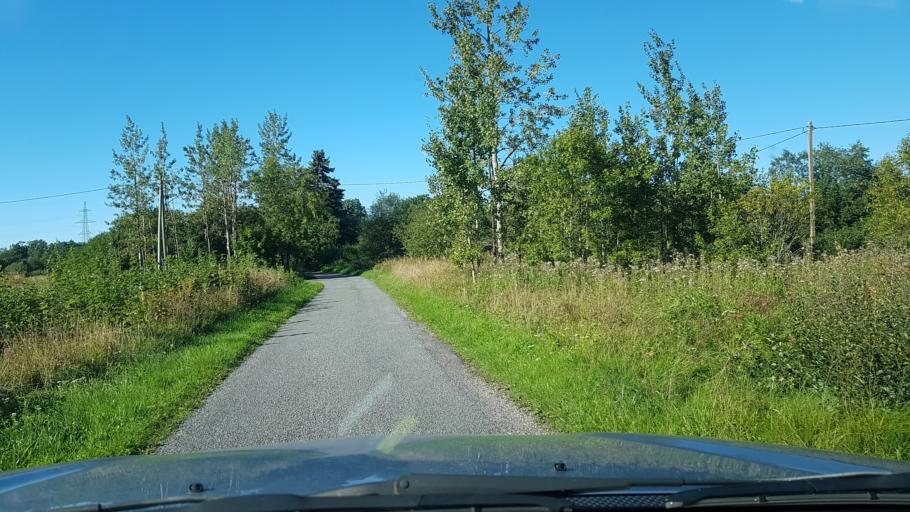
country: EE
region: Harju
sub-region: Joelaehtme vald
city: Loo
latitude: 59.4275
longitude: 24.9324
